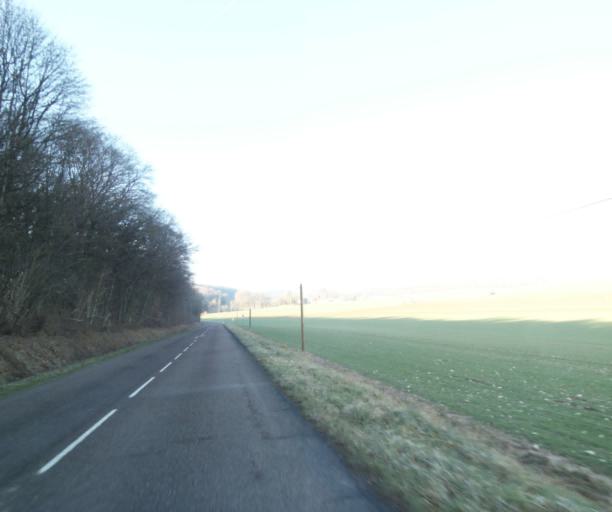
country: FR
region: Champagne-Ardenne
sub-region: Departement de la Haute-Marne
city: Chevillon
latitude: 48.5524
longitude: 5.0920
